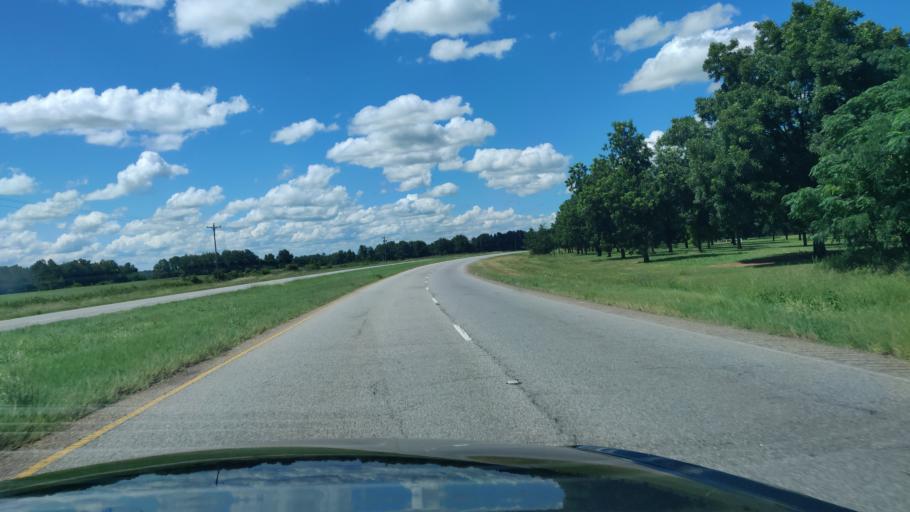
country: US
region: Georgia
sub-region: Stewart County
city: Richland
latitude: 32.0372
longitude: -84.6777
